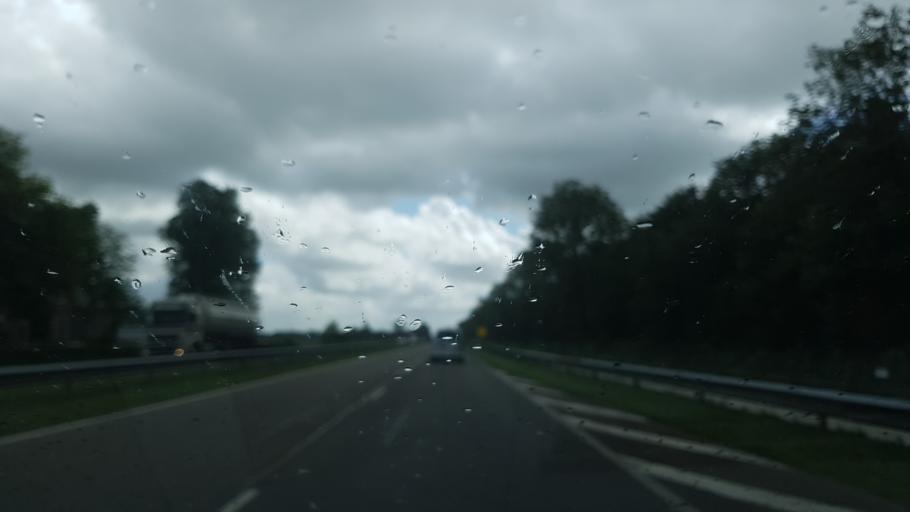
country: NL
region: Friesland
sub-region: Gemeente Tytsjerksteradiel
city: Tytsjerk
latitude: 53.2179
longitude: 5.8904
